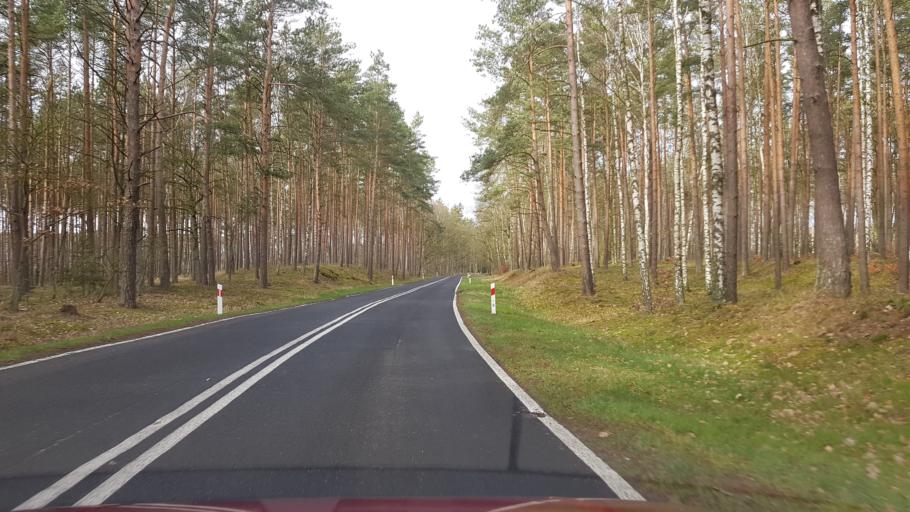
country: PL
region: West Pomeranian Voivodeship
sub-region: Powiat policki
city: Nowe Warpno
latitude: 53.6809
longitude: 14.3566
